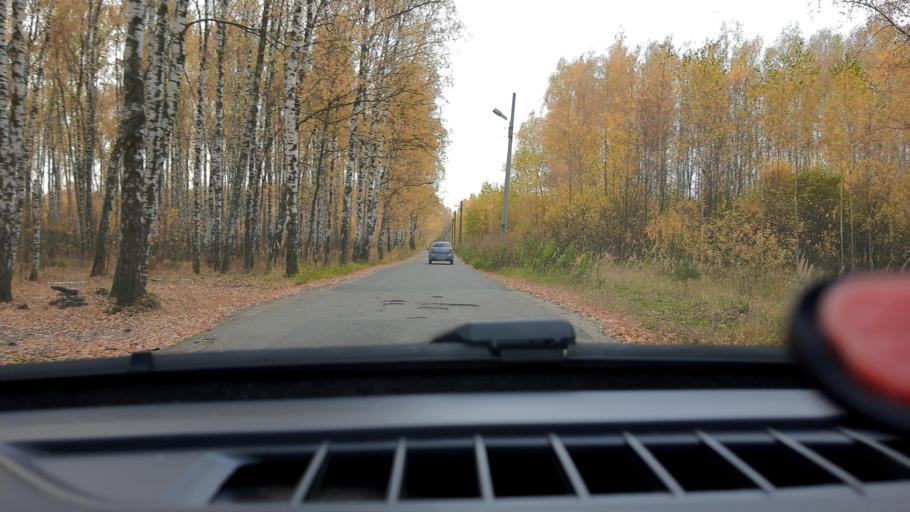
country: RU
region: Nizjnij Novgorod
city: Gorbatovka
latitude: 56.2899
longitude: 43.8312
